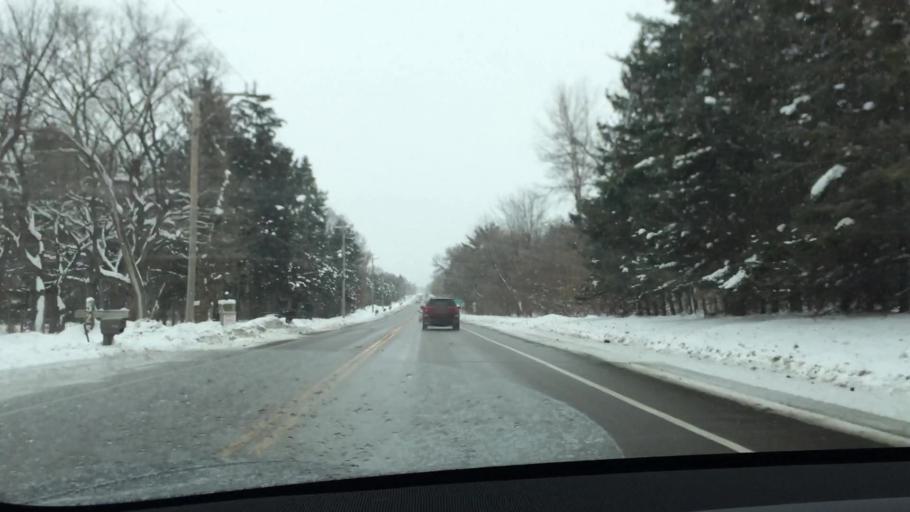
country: US
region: Minnesota
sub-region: Ramsey County
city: Shoreview
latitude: 45.1002
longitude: -93.1272
